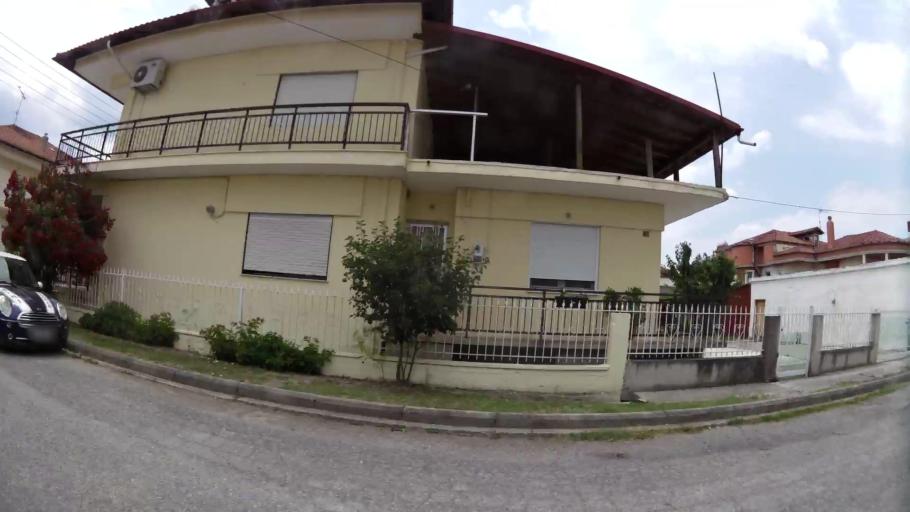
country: GR
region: Central Macedonia
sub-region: Nomos Pierias
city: Kallithea
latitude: 40.2718
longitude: 22.5797
